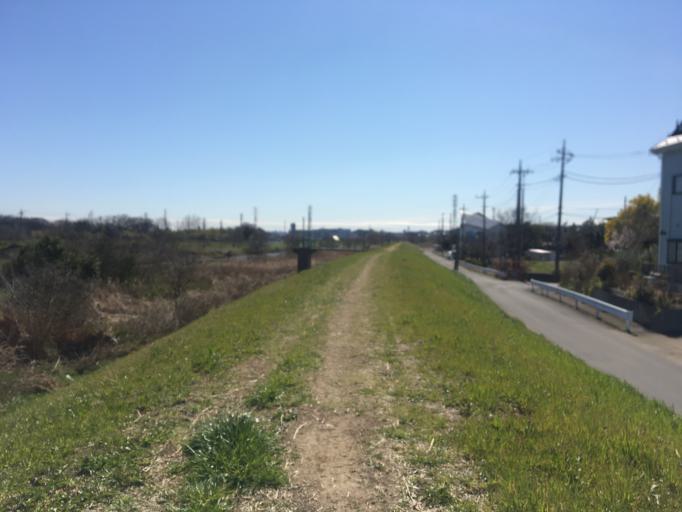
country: JP
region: Saitama
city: Asaka
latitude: 35.8186
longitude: 139.6081
